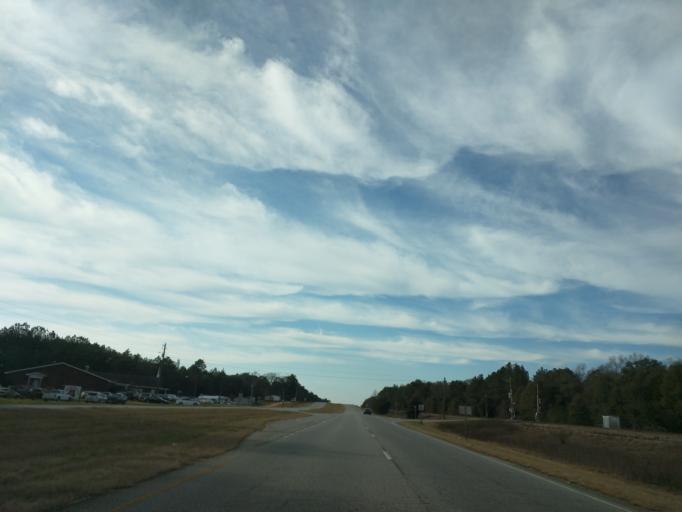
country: US
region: Georgia
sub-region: Decatur County
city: Bainbridge
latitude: 30.8982
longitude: -84.5140
